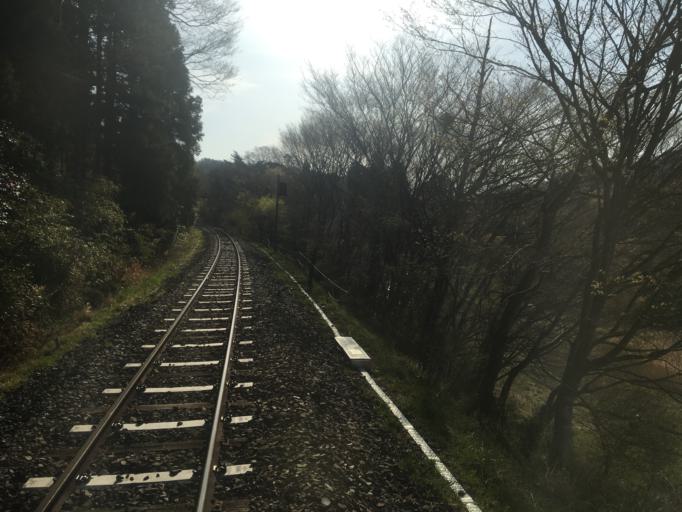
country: JP
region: Iwate
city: Ofunato
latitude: 39.0534
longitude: 141.7946
